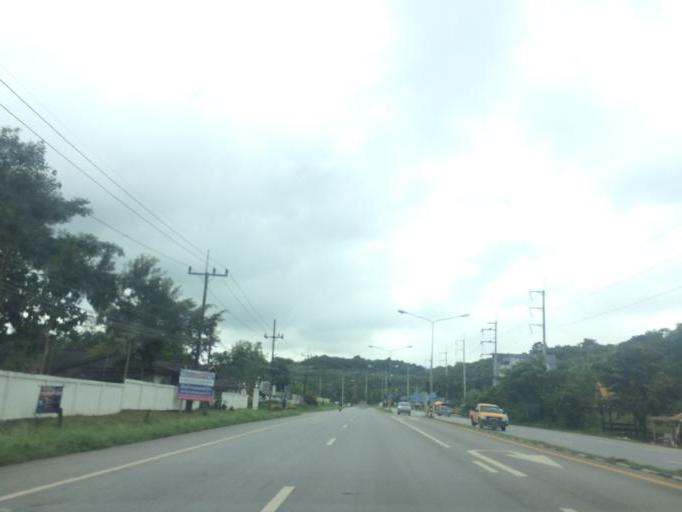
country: TH
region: Chiang Rai
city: Mae Chan
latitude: 20.1126
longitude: 99.8732
